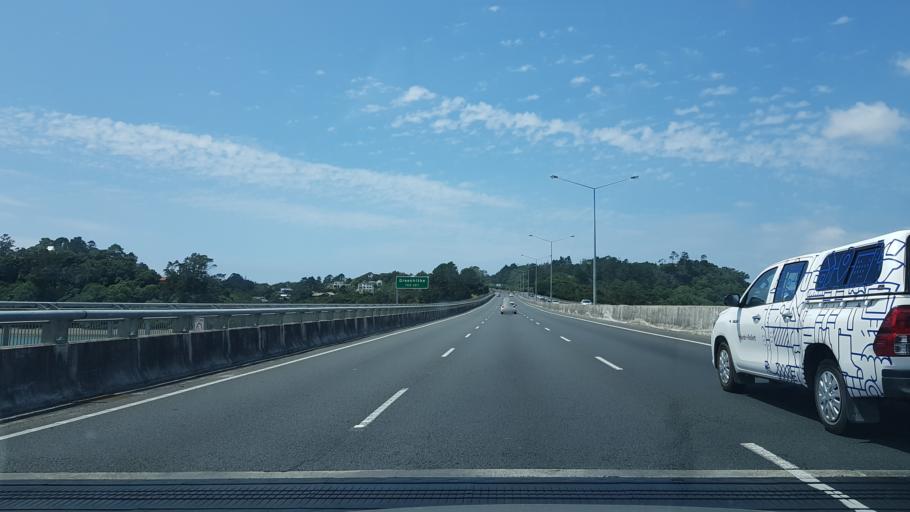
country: NZ
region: Auckland
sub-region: Auckland
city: North Shore
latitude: -36.7856
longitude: 174.6652
